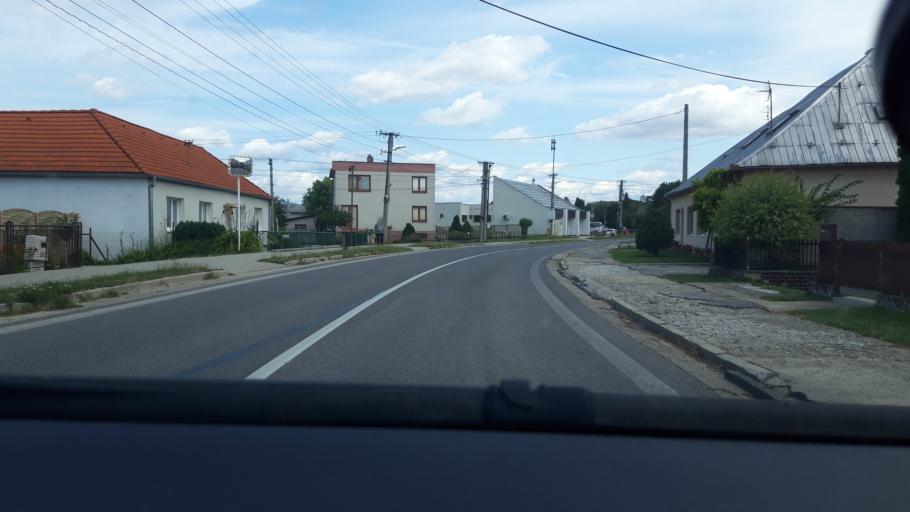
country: SK
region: Trenciansky
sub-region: Okres Nove Mesto nad Vahom
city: Nove Mesto nad Vahom
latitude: 48.7864
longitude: 17.8939
